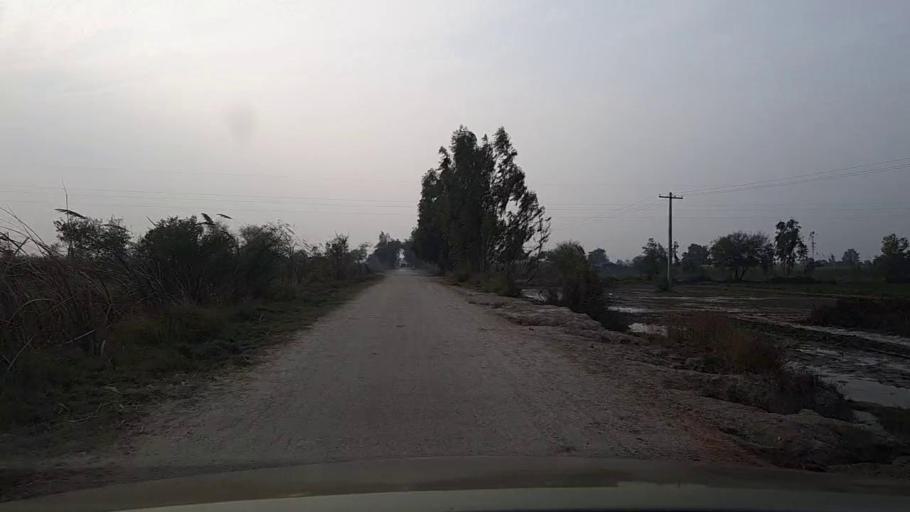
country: PK
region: Sindh
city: Sanghar
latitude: 26.2176
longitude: 68.9517
